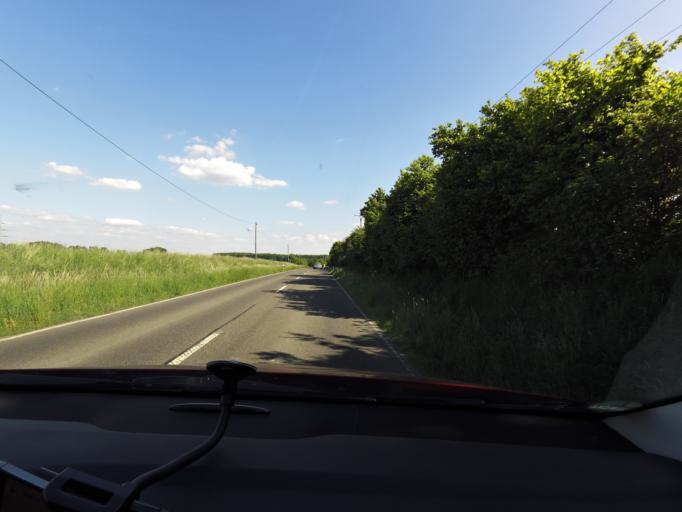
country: DE
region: Rheinland-Pfalz
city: Dernau
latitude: 50.5769
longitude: 7.0524
